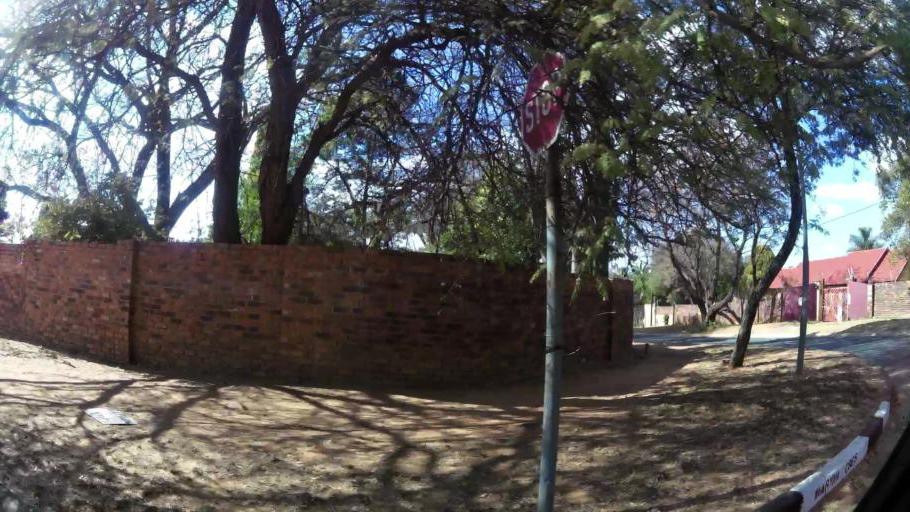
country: ZA
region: Gauteng
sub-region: City of Johannesburg Metropolitan Municipality
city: Roodepoort
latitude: -26.0747
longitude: 27.9685
